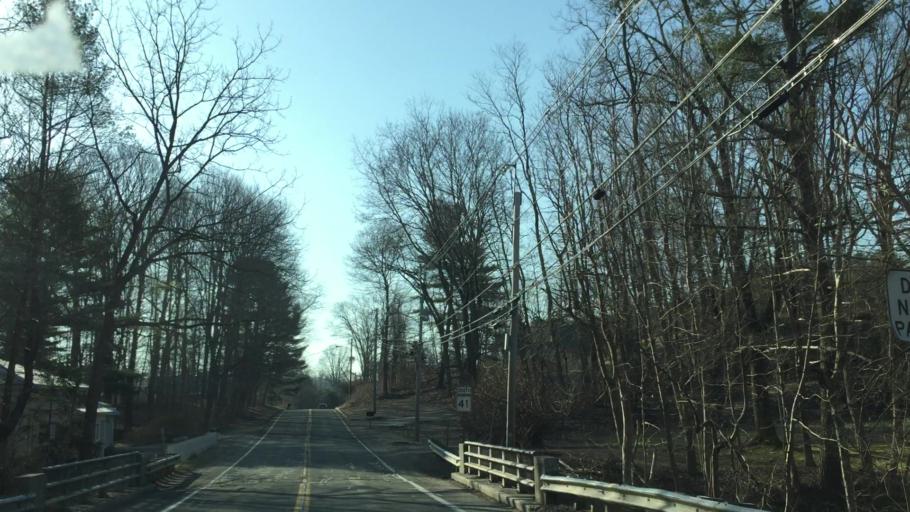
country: US
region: Massachusetts
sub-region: Berkshire County
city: Housatonic
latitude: 42.2272
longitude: -73.3637
